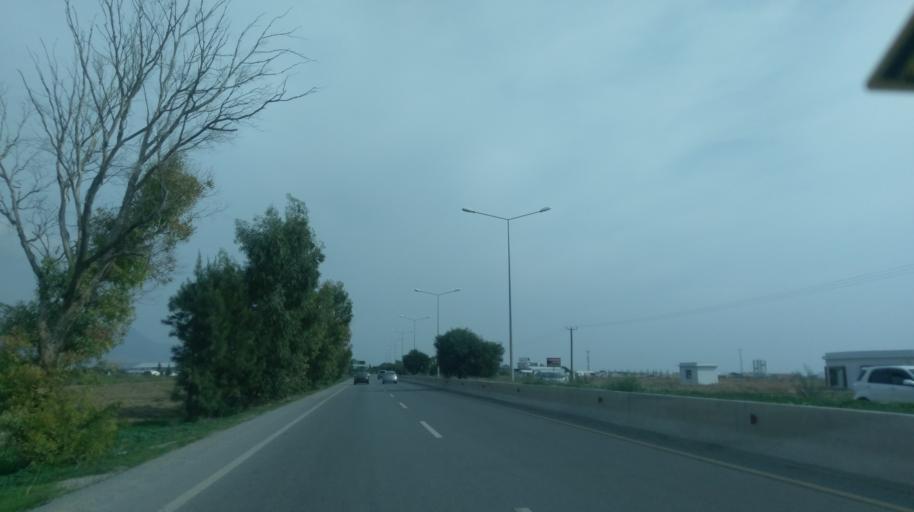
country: CY
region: Lefkosia
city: Nicosia
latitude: 35.2168
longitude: 33.4549
